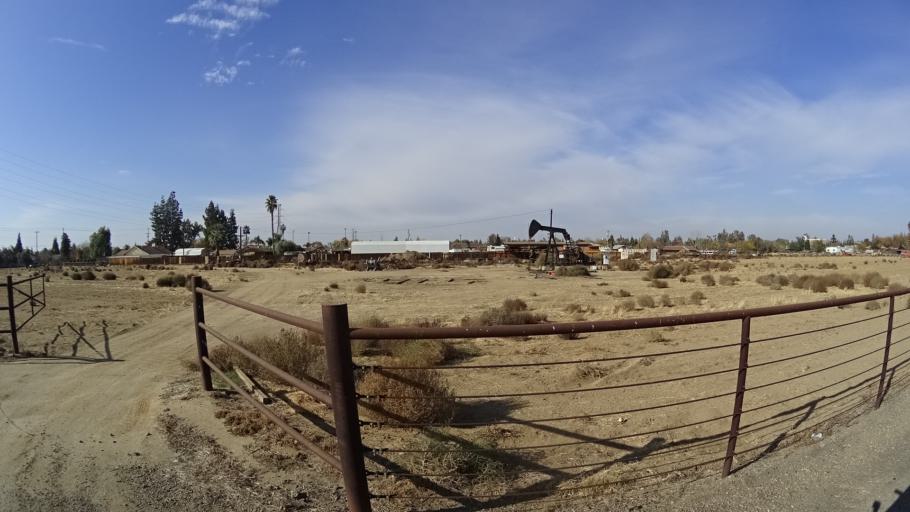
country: US
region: California
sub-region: Kern County
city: Greenacres
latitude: 35.3989
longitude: -119.0689
